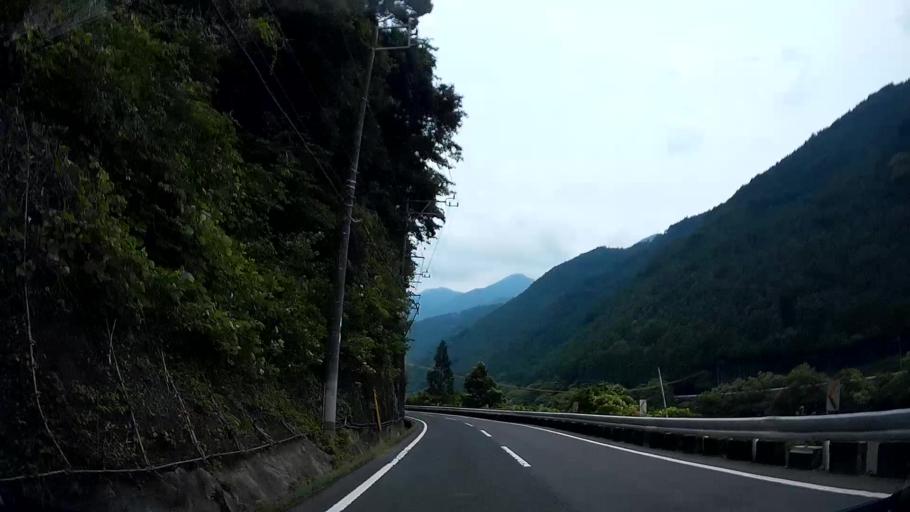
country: JP
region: Shizuoka
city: Mori
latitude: 35.0273
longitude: 137.8442
